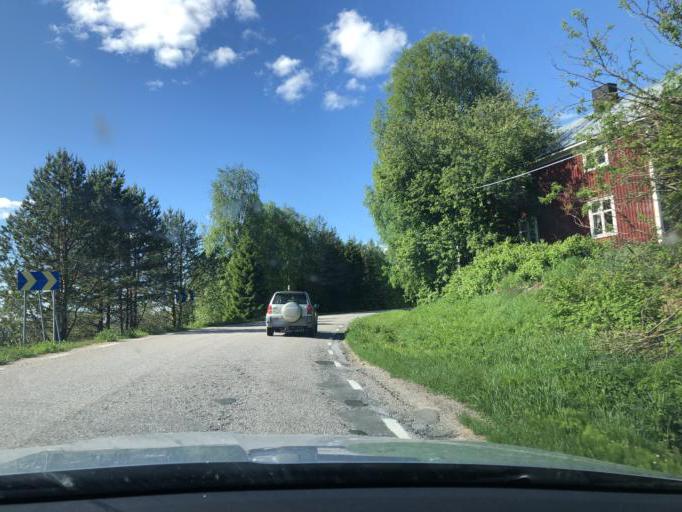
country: SE
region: Norrbotten
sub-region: Kalix Kommun
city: Kalix
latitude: 65.9992
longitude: 23.1431
